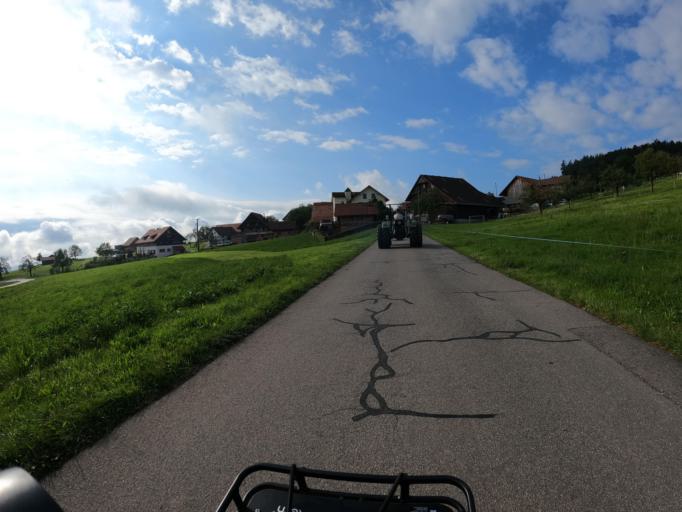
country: CH
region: Aargau
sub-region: Bezirk Muri
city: Buttwil
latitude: 47.2333
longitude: 8.3279
